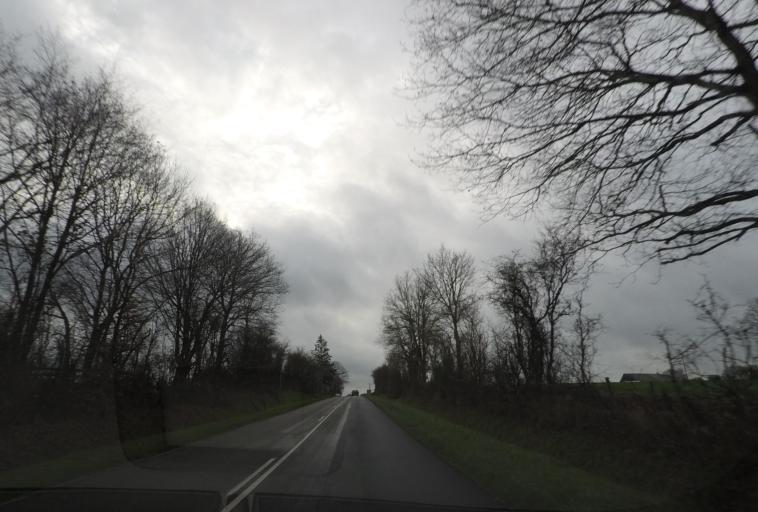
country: FR
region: Pays de la Loire
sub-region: Departement de la Sarthe
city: Vibraye
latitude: 48.0210
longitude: 0.7523
